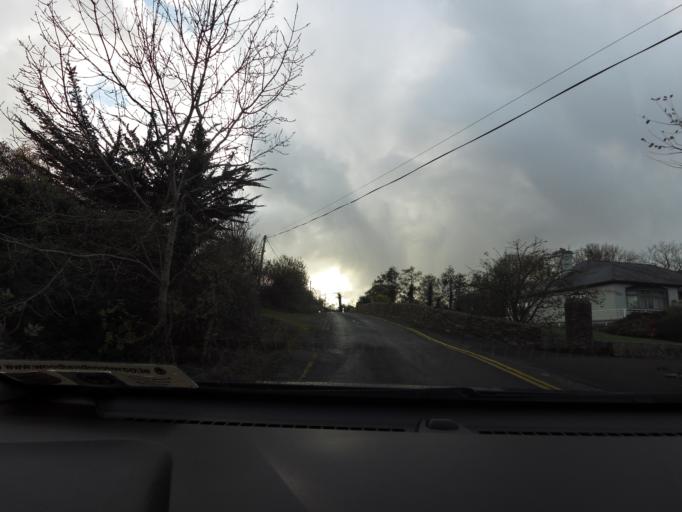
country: IE
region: Connaught
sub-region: Maigh Eo
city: Westport
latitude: 53.7754
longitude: -9.7722
